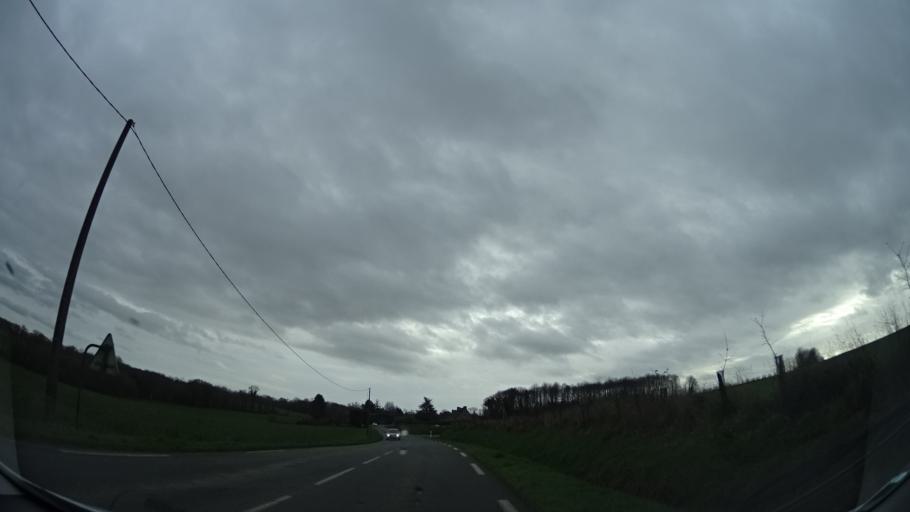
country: FR
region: Brittany
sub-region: Departement des Cotes-d'Armor
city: Les Champs-Geraux
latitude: 48.4145
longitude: -1.9972
